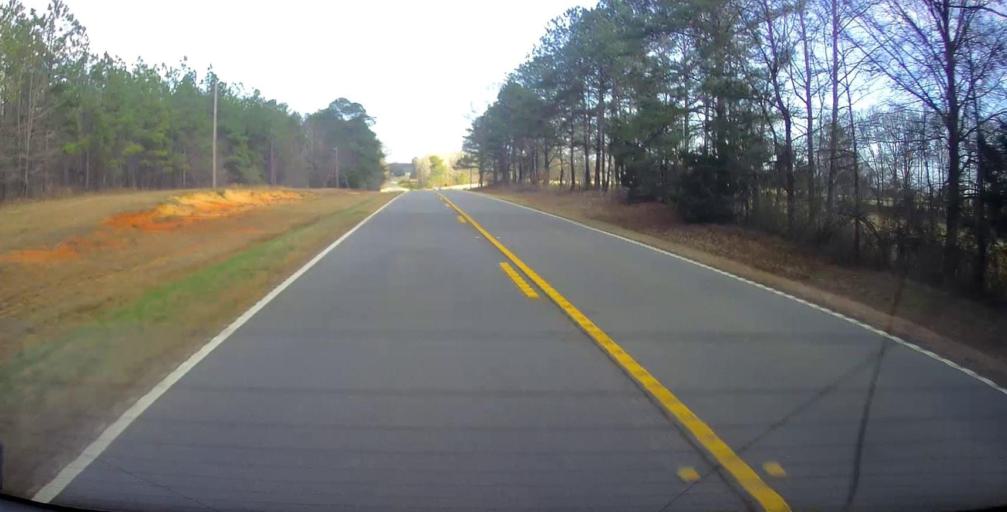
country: US
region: Georgia
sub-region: Harris County
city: Hamilton
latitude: 32.6856
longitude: -84.7686
